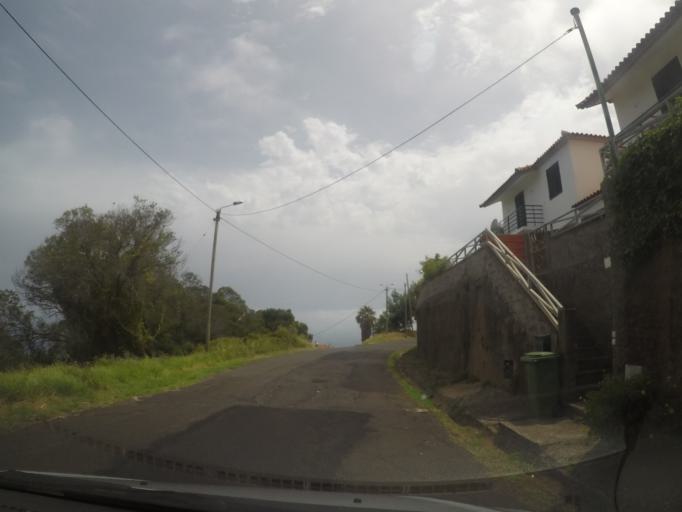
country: PT
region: Madeira
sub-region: Machico
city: Machico
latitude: 32.7023
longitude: -16.7865
